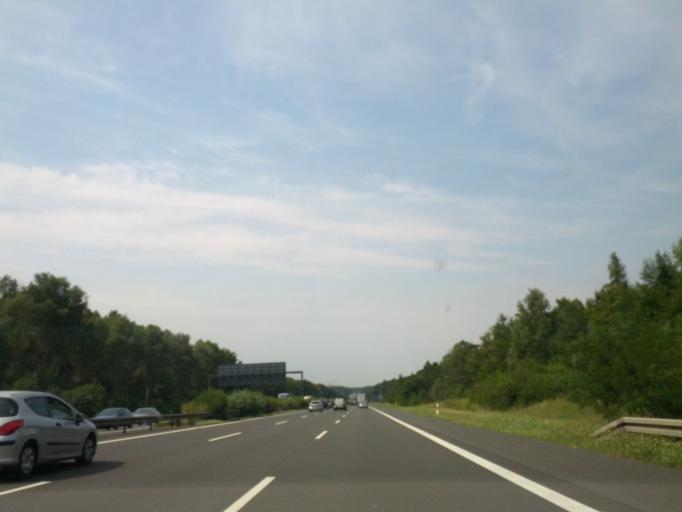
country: DE
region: Brandenburg
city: Fichtenwalde
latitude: 52.2985
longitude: 12.9001
